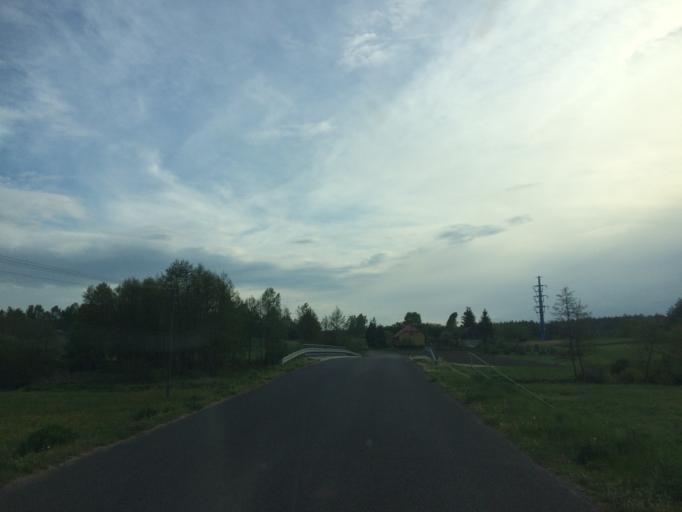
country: PL
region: Warmian-Masurian Voivodeship
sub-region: Powiat ilawski
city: Lubawa
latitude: 53.4301
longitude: 19.6917
